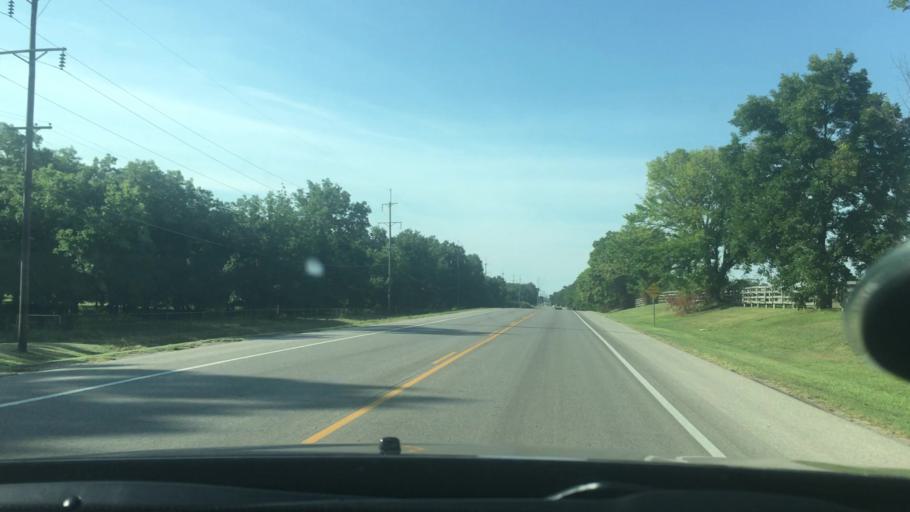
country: US
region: Oklahoma
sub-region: Garvin County
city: Pauls Valley
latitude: 34.6904
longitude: -97.2129
